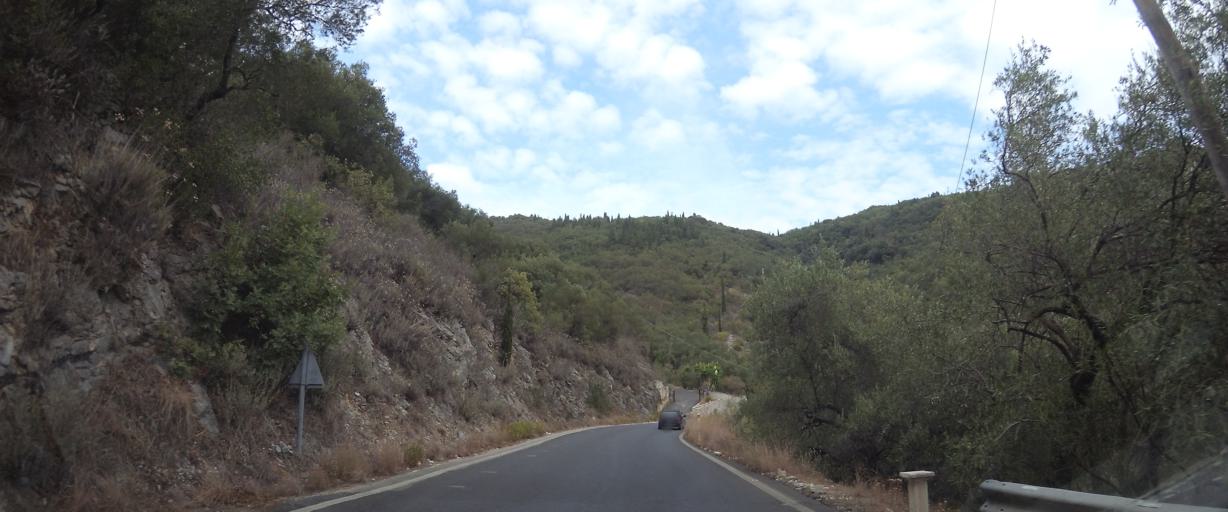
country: GR
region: Ionian Islands
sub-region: Nomos Kerkyras
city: Kontokali
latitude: 39.7312
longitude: 19.9118
